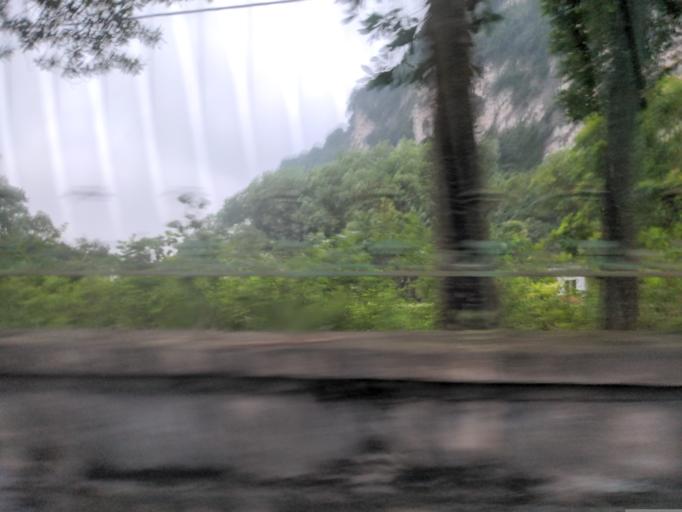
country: VN
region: Ninh Binh
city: Thi Tran Tam Diep
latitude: 20.2098
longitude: 105.9073
